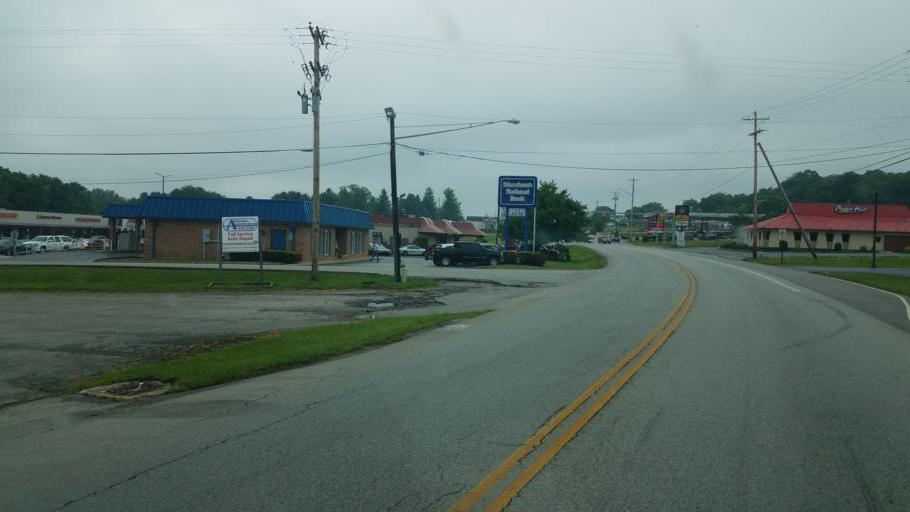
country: US
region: Ohio
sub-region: Highland County
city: Hillsboro
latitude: 39.2305
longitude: -83.6108
